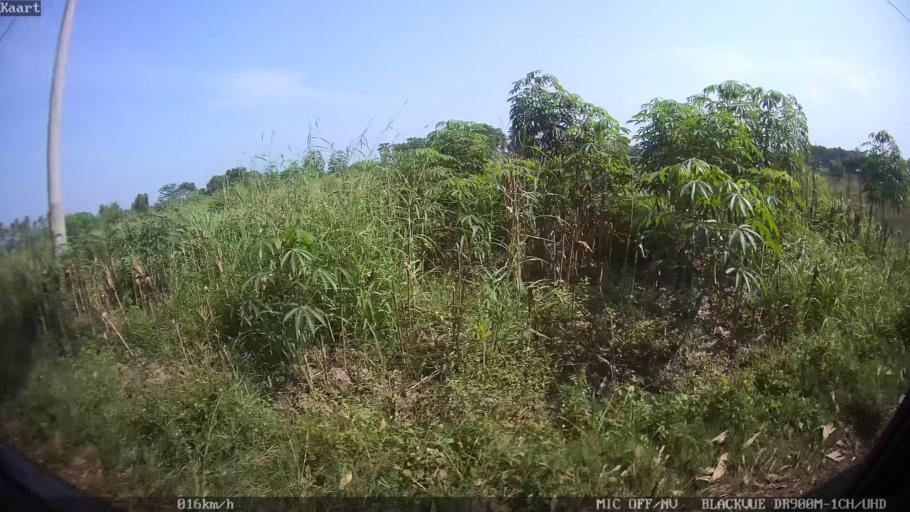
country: ID
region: Lampung
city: Natar
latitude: -5.2642
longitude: 105.2087
